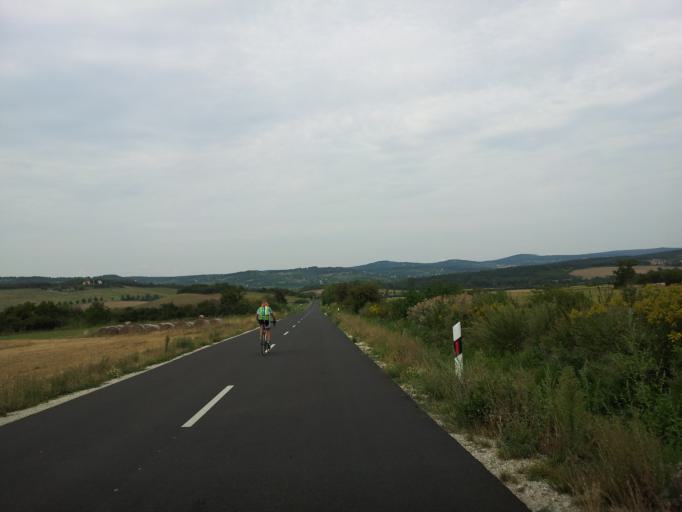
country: HU
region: Veszprem
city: Balatonfured
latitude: 46.9407
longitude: 17.7780
